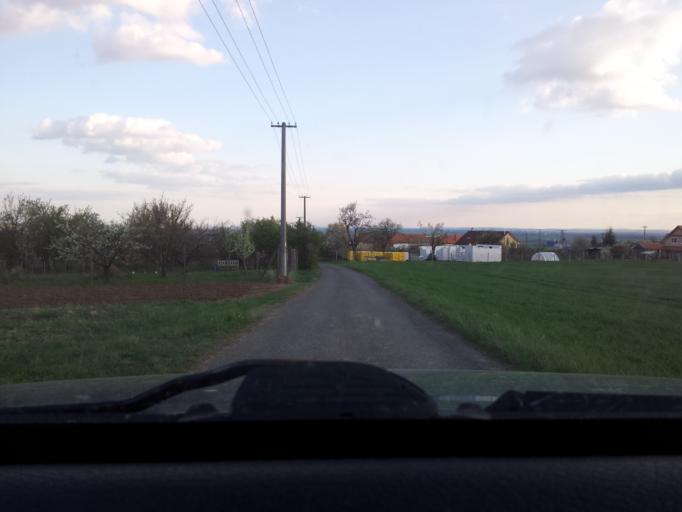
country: SK
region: Nitriansky
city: Tlmace
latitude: 48.3012
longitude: 18.5609
